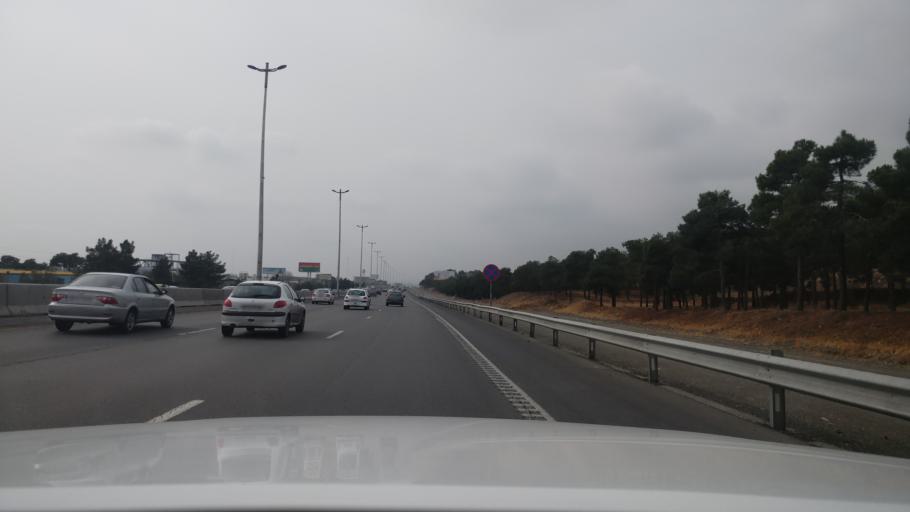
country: IR
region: Tehran
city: Shahr-e Qods
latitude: 35.7178
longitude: 51.2308
